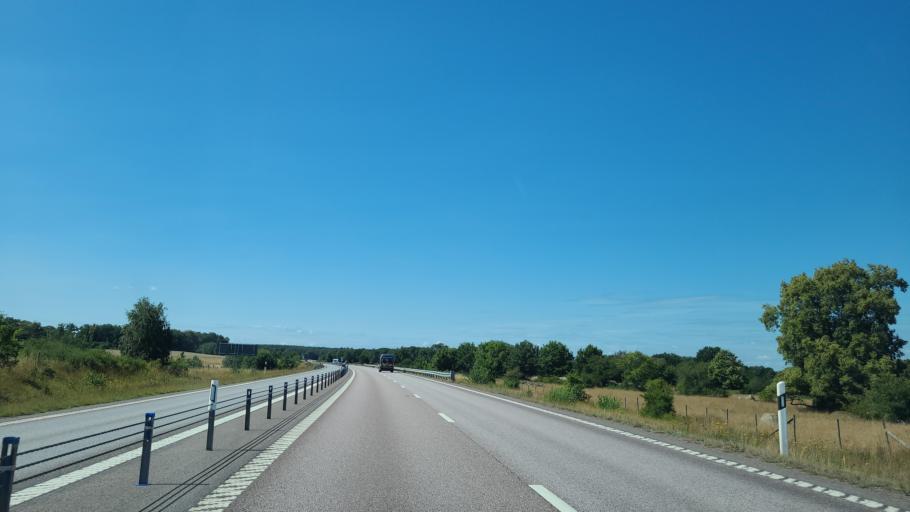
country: SE
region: Kalmar
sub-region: Kalmar Kommun
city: Ljungbyholm
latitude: 56.6155
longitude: 16.1511
